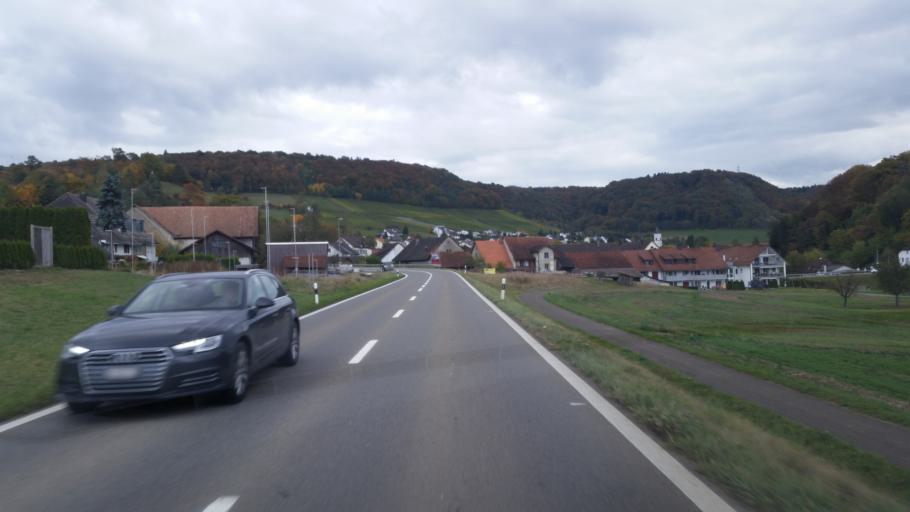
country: CH
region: Aargau
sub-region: Bezirk Zurzach
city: Tegerfelden
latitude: 47.5617
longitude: 8.2828
